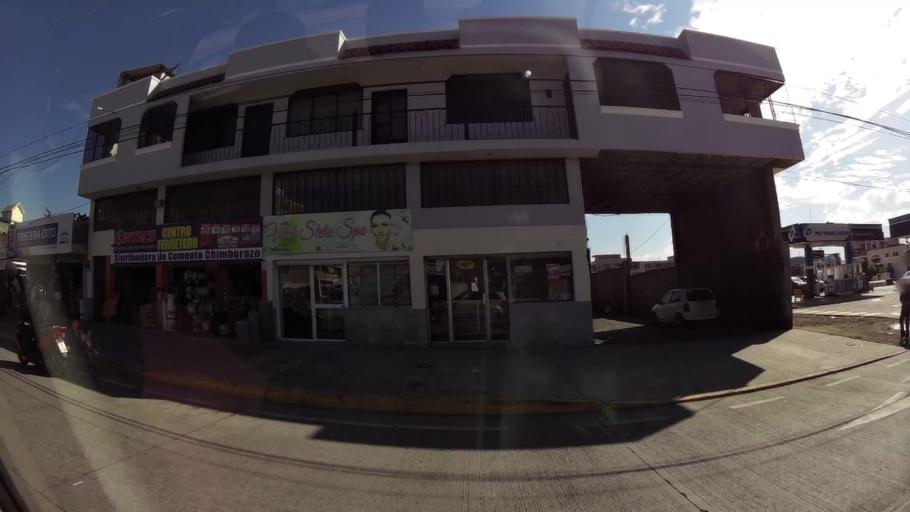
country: EC
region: Chimborazo
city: Riobamba
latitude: -1.6529
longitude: -78.6672
